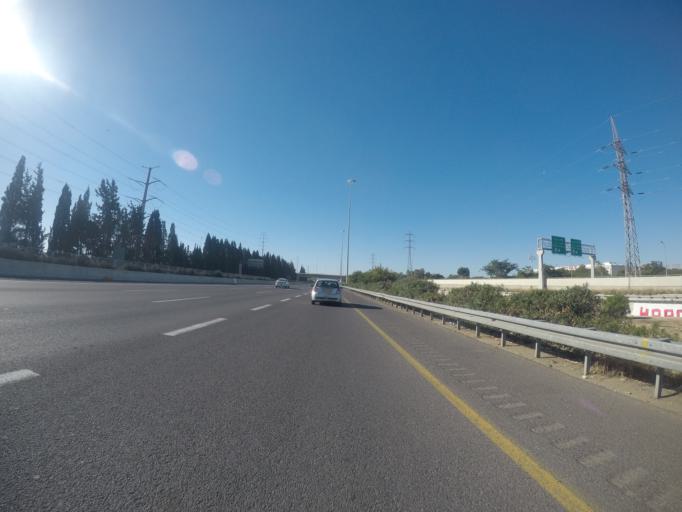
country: IL
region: Central District
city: Bet Dagan
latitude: 32.0020
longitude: 34.8073
